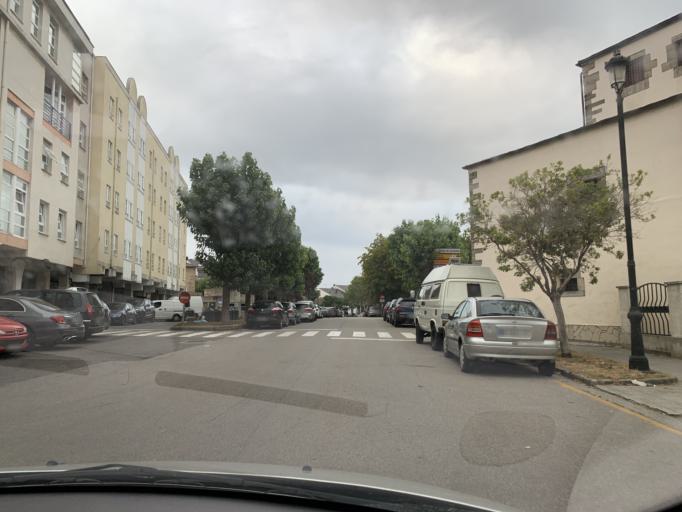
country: ES
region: Galicia
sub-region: Provincia de Lugo
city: Ribadeo
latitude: 43.5348
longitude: -7.0403
